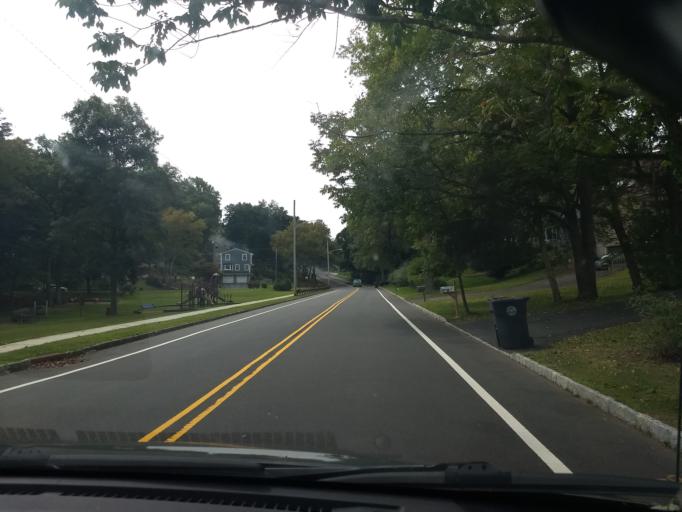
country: US
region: New Jersey
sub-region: Morris County
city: Morristown
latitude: 40.8096
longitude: -74.5060
